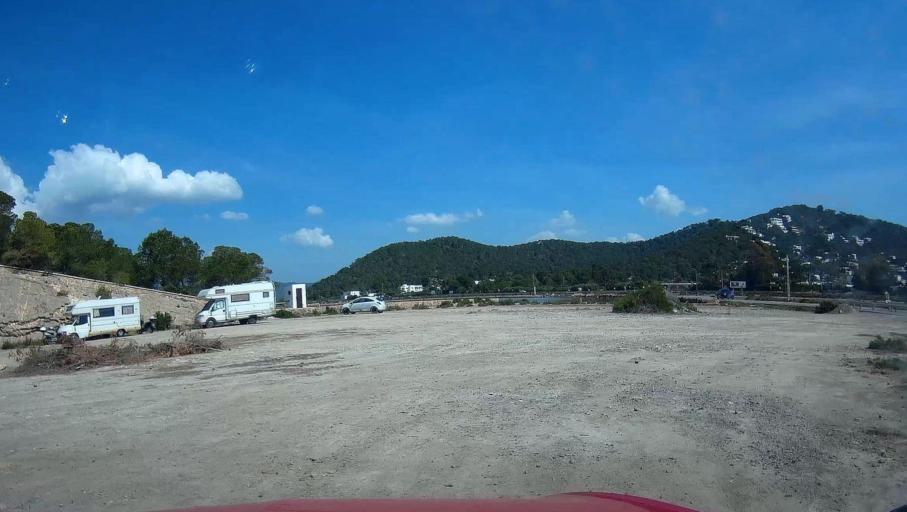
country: ES
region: Balearic Islands
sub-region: Illes Balears
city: Ibiza
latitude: 38.8492
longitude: 1.3883
